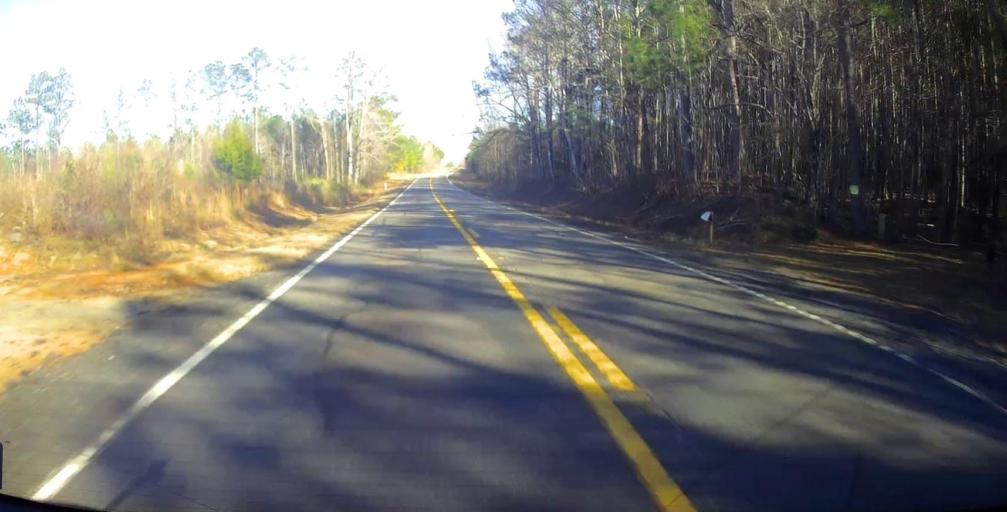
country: US
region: Georgia
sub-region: Talbot County
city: Talbotton
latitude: 32.6724
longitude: -84.4859
